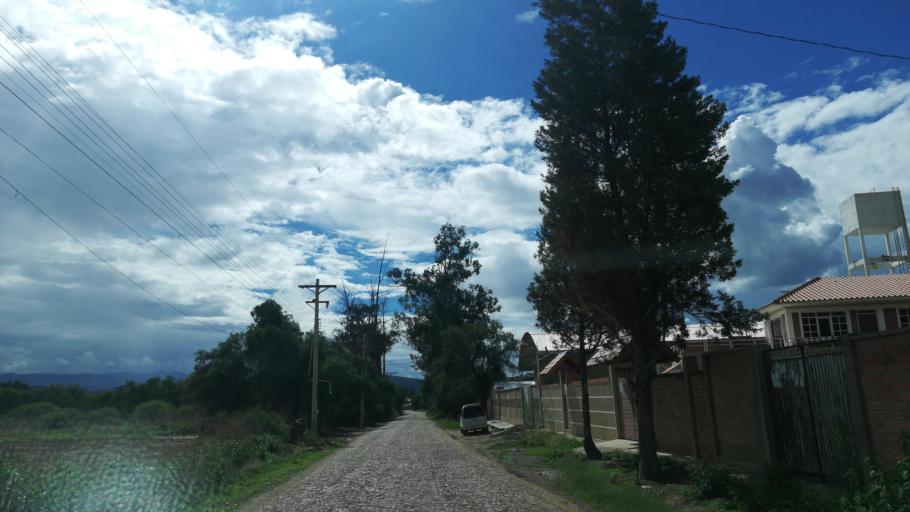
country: BO
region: Cochabamba
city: Capinota
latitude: -17.5494
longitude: -66.2349
